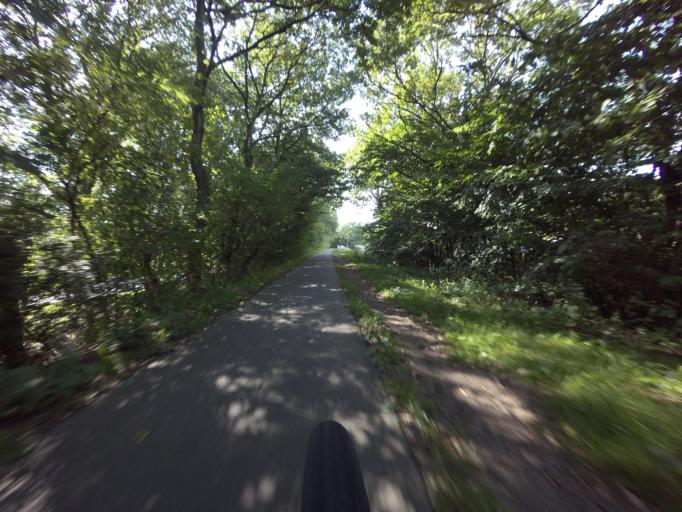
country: DK
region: Central Jutland
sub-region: Viborg Kommune
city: Viborg
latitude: 56.4015
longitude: 9.3534
